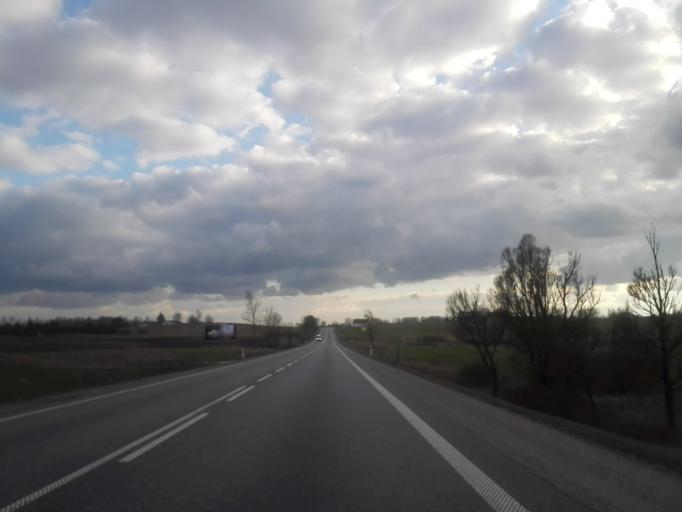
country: PL
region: Podlasie
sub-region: Suwalki
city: Suwalki
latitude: 54.2066
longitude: 23.0248
